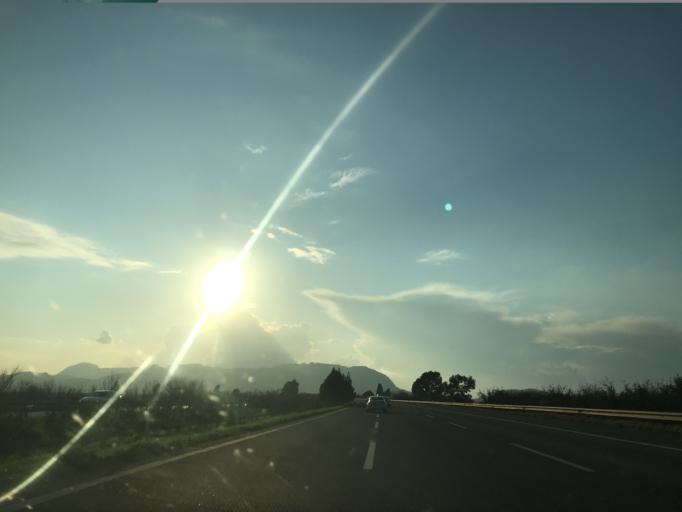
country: TR
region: Adana
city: Ceyhan
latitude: 36.9852
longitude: 35.8053
